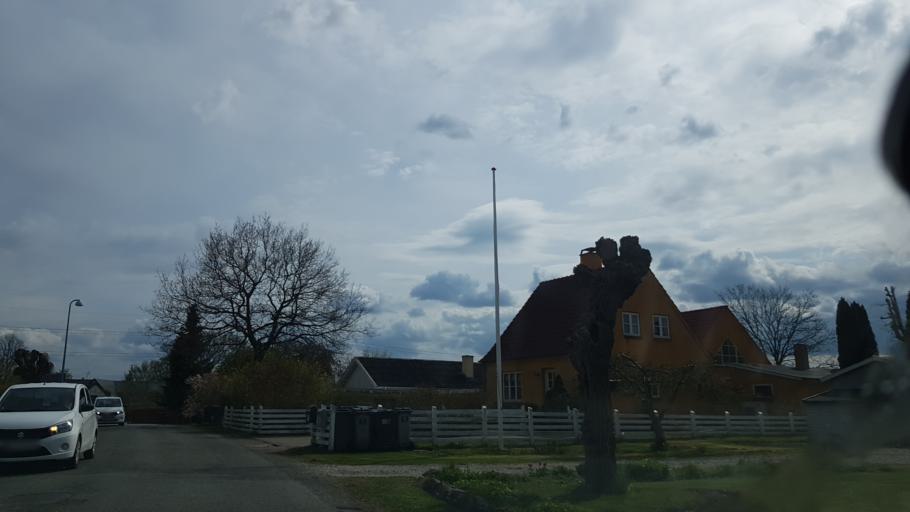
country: DK
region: Capital Region
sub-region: Allerod Kommune
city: Lillerod
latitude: 55.8921
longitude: 12.3281
